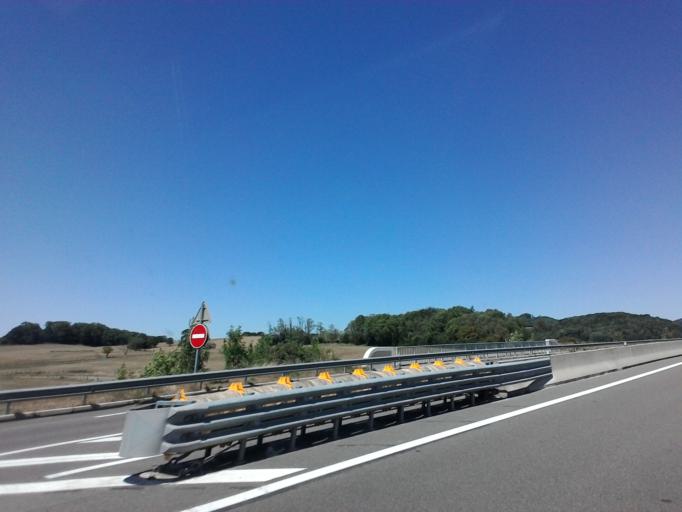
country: FR
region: Franche-Comte
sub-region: Departement du Jura
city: Montmorot
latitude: 46.6929
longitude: 5.5281
